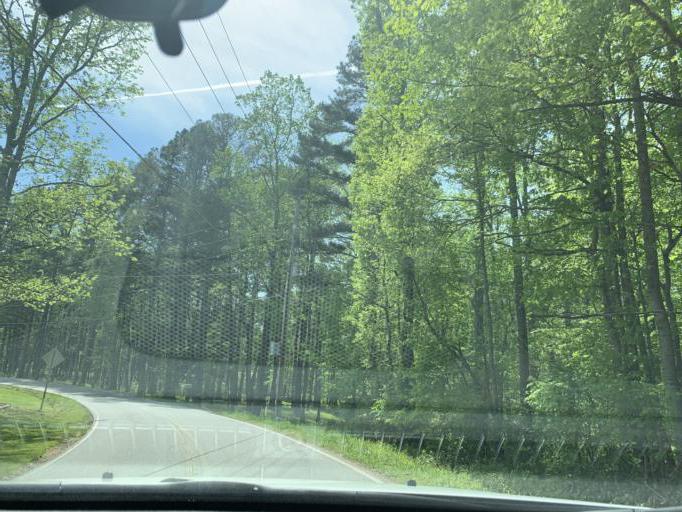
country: US
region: Georgia
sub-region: Forsyth County
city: Cumming
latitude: 34.2514
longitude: -84.2049
